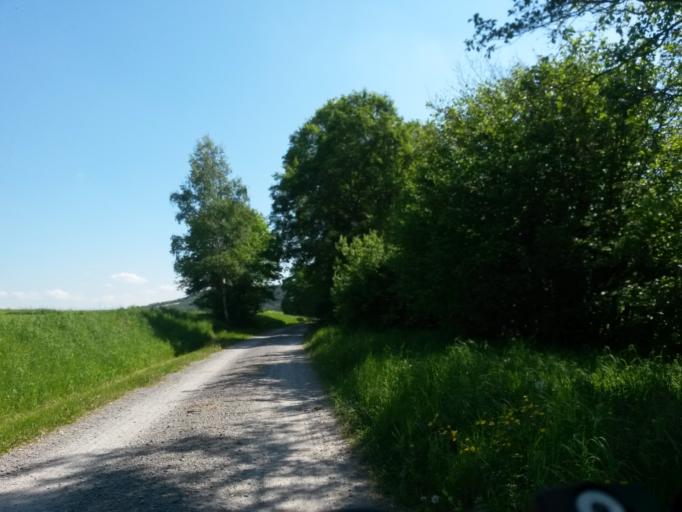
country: DE
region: Bavaria
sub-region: Regierungsbezirk Unterfranken
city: Bad Bocklet
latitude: 50.2778
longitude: 10.0914
